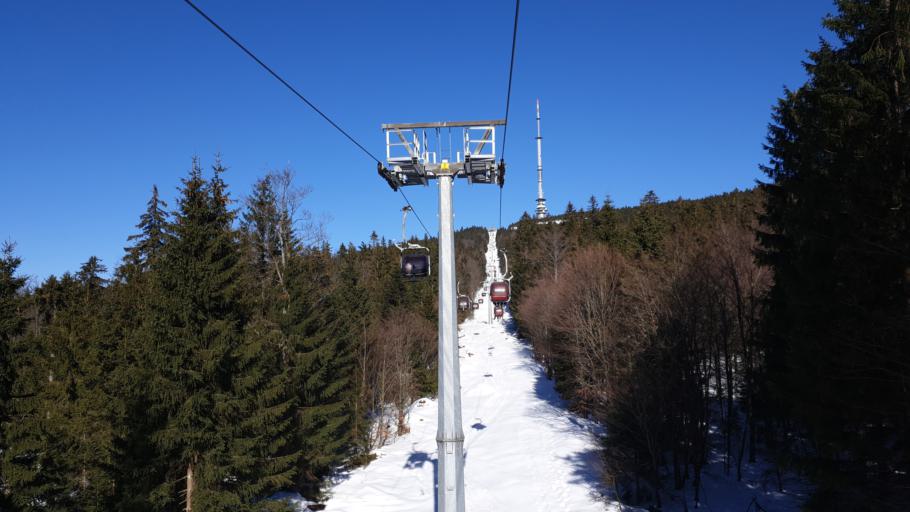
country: DE
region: Bavaria
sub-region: Upper Franconia
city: Bischofsgrun
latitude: 50.0209
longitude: 11.8082
